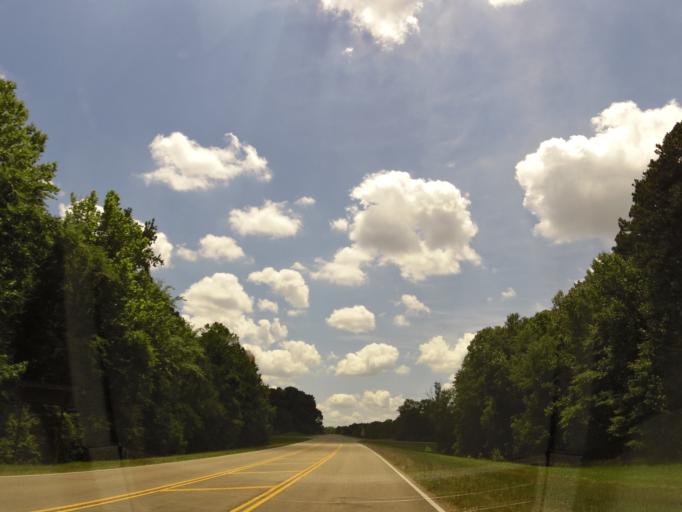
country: US
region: Mississippi
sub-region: Lee County
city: Tupelo
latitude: 34.3039
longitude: -88.7231
